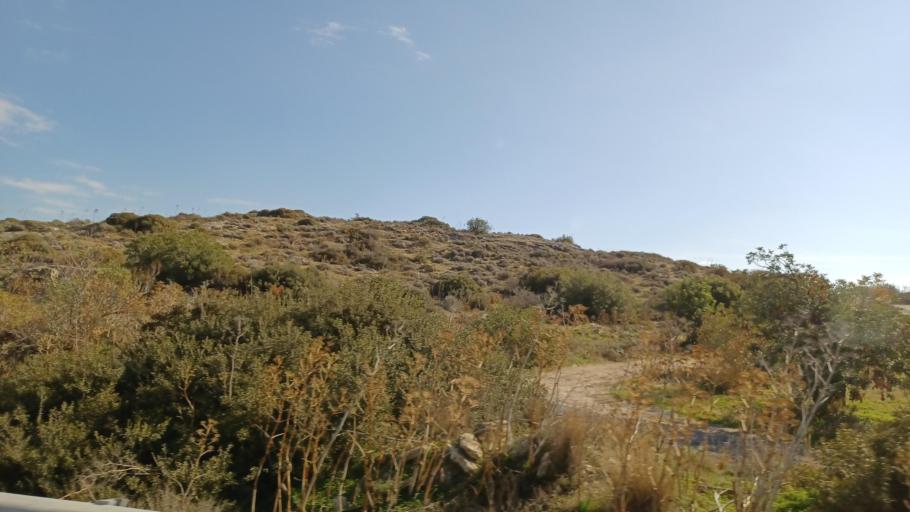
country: CY
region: Larnaka
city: Kofinou
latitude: 34.7678
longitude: 33.3267
